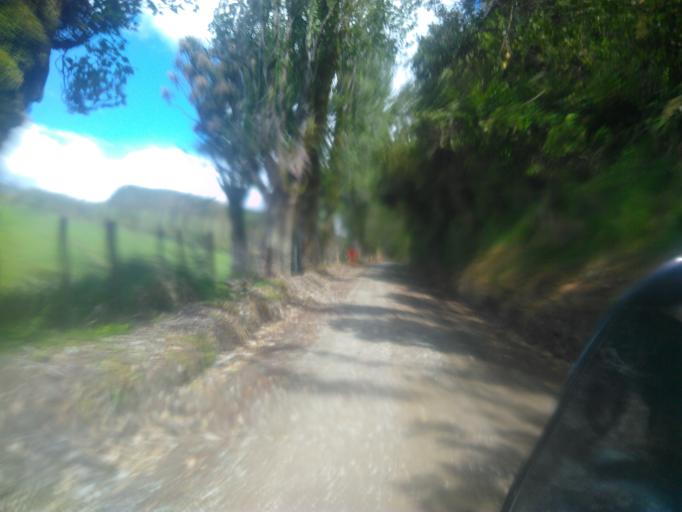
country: NZ
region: Hawke's Bay
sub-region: Wairoa District
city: Wairoa
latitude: -38.7675
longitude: 177.5947
